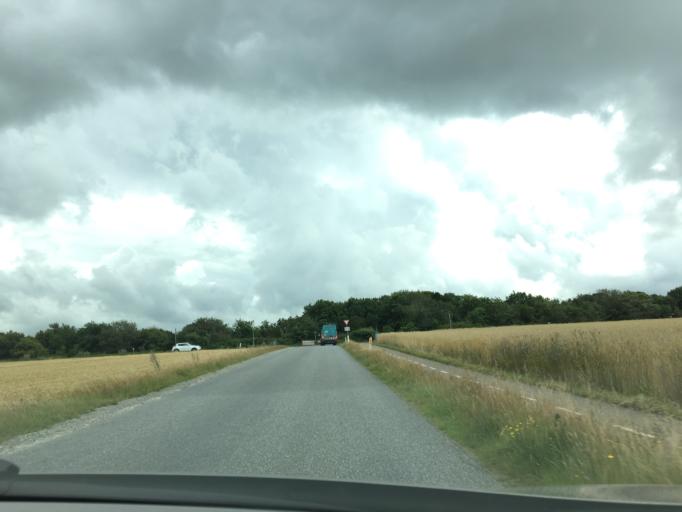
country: DK
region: South Denmark
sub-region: Varde Kommune
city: Oksbol
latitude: 55.7264
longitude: 8.2672
